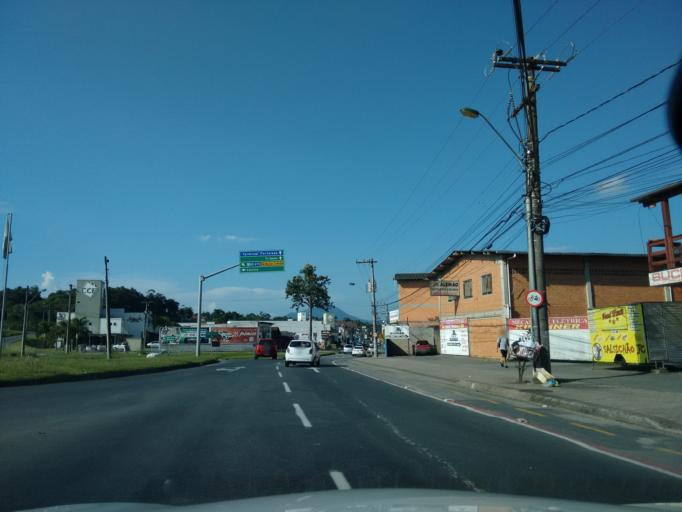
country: BR
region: Santa Catarina
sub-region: Blumenau
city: Blumenau
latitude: -26.8822
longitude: -49.0690
